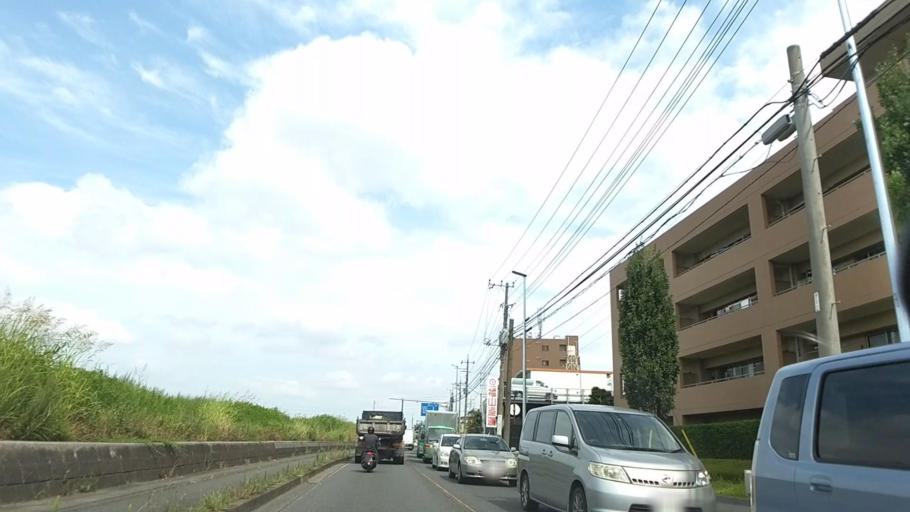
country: JP
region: Kanagawa
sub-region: Kawasaki-shi
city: Kawasaki
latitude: 35.5327
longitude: 139.6687
